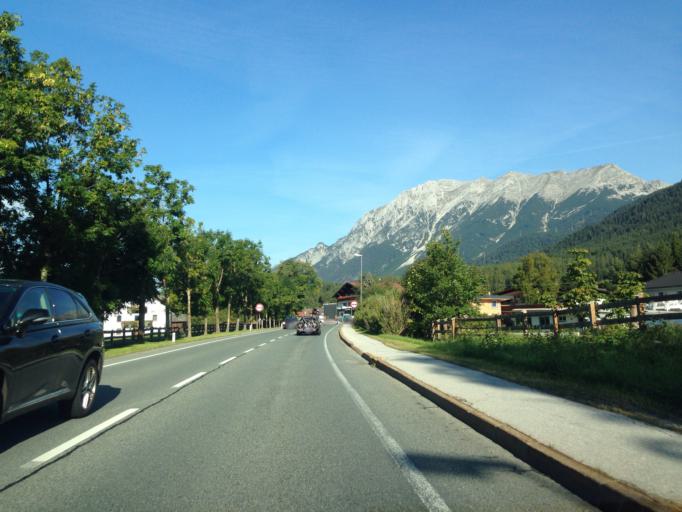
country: AT
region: Tyrol
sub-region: Politischer Bezirk Imst
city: Obsteig
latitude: 47.2987
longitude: 10.9243
